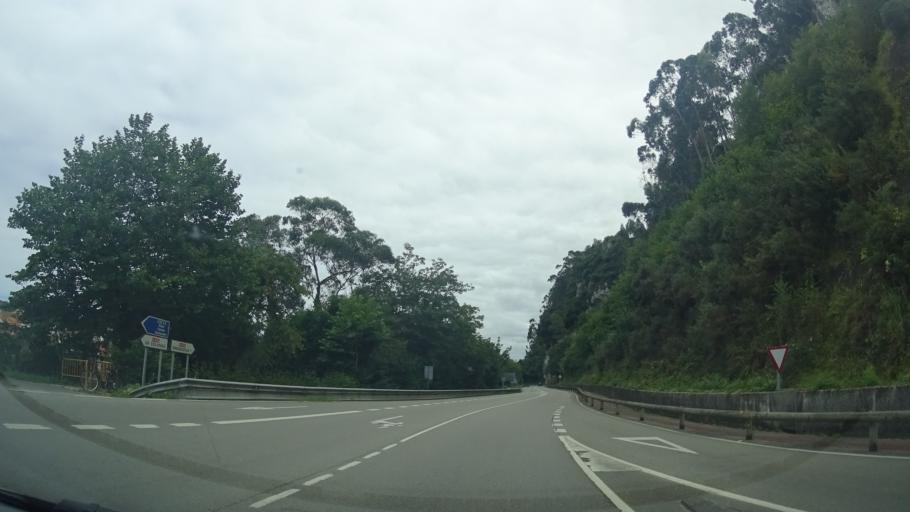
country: ES
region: Asturias
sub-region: Province of Asturias
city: Ribadesella
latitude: 43.4634
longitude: -5.0723
